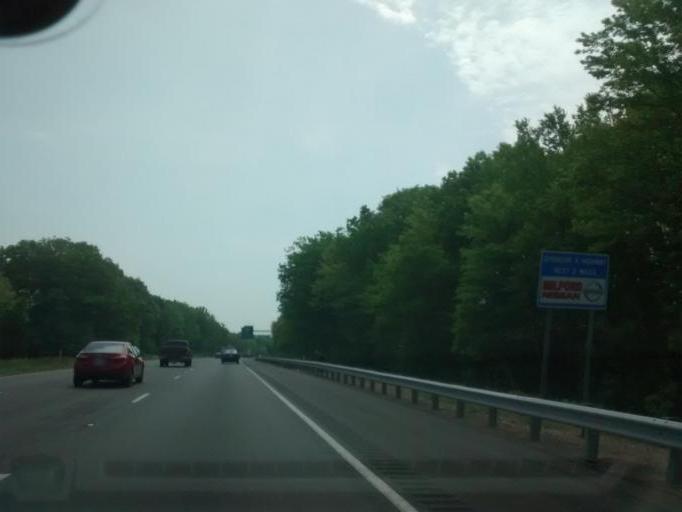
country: US
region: Massachusetts
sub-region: Worcester County
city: Milford
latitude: 42.1624
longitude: -71.4995
